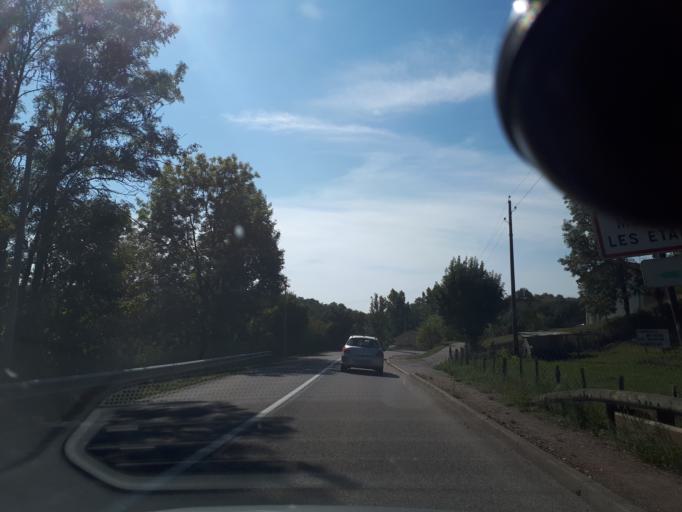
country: FR
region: Rhone-Alpes
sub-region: Departement de l'Isere
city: Chatonnay
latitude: 45.5171
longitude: 5.2109
